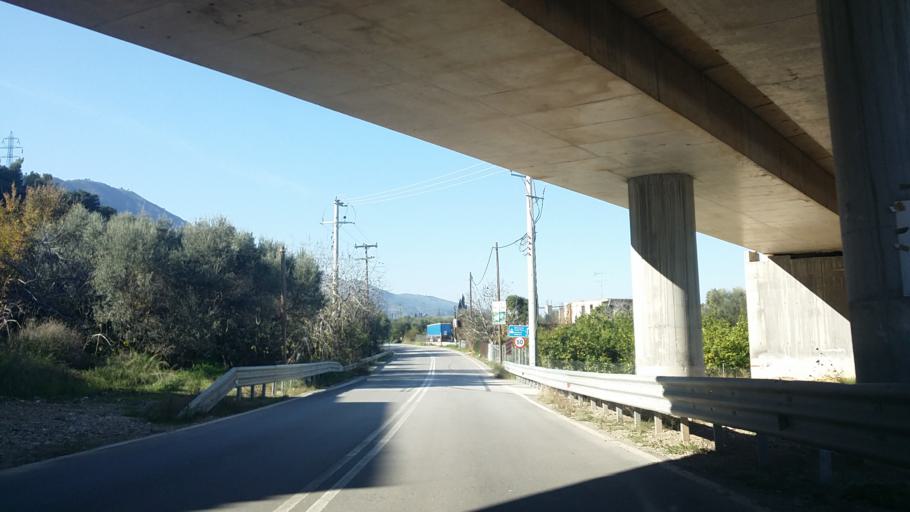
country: GR
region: West Greece
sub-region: Nomos Achaias
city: Temeni
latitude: 38.1827
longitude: 22.2075
